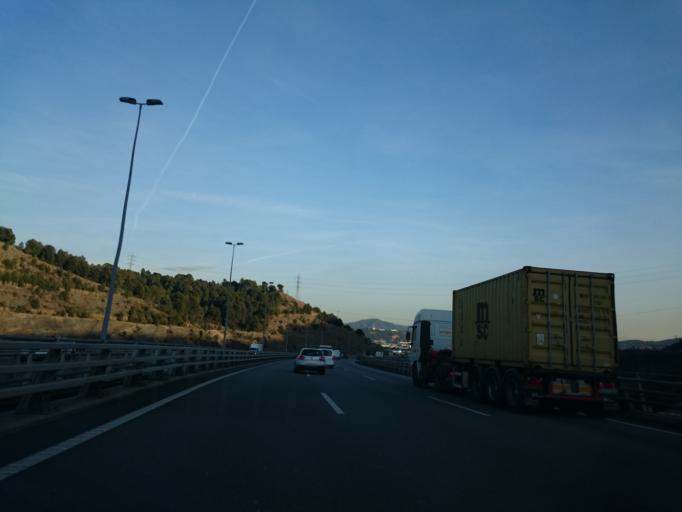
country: ES
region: Catalonia
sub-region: Provincia de Barcelona
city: Martorell
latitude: 41.4731
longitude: 1.9374
